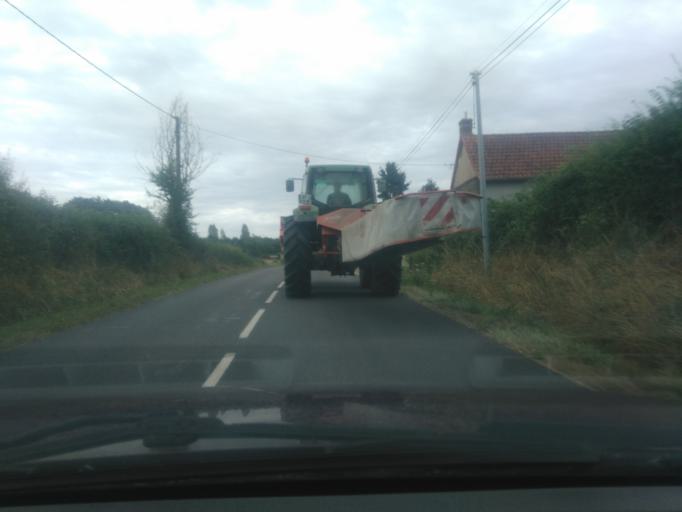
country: FR
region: Bourgogne
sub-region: Departement de la Nievre
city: Dornes
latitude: 46.7718
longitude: 3.3078
